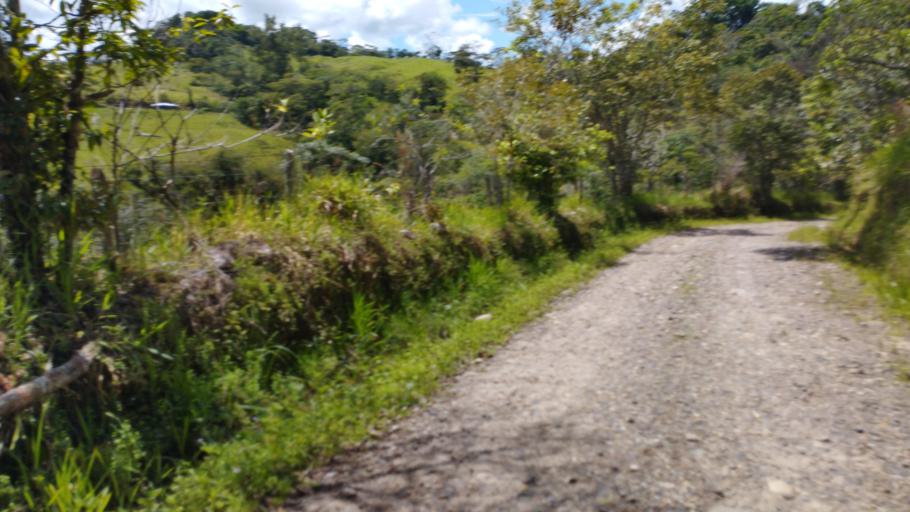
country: CO
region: Boyaca
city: San Luis de Gaceno
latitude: 4.7743
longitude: -73.1351
